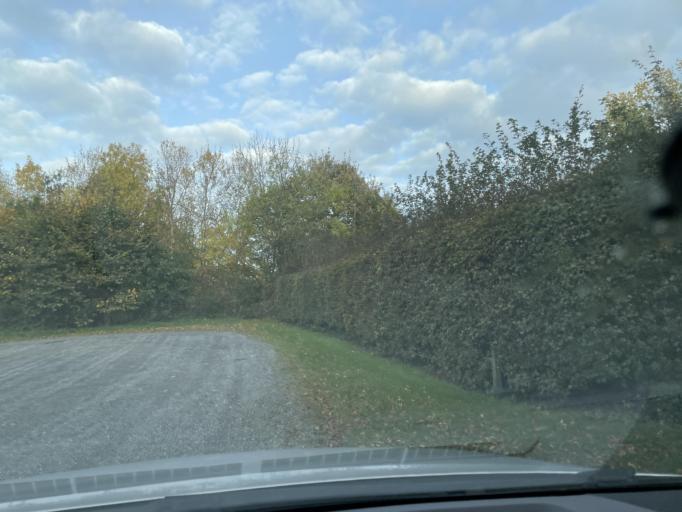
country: DK
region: South Denmark
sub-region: Kerteminde Kommune
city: Kerteminde
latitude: 55.4365
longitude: 10.6867
